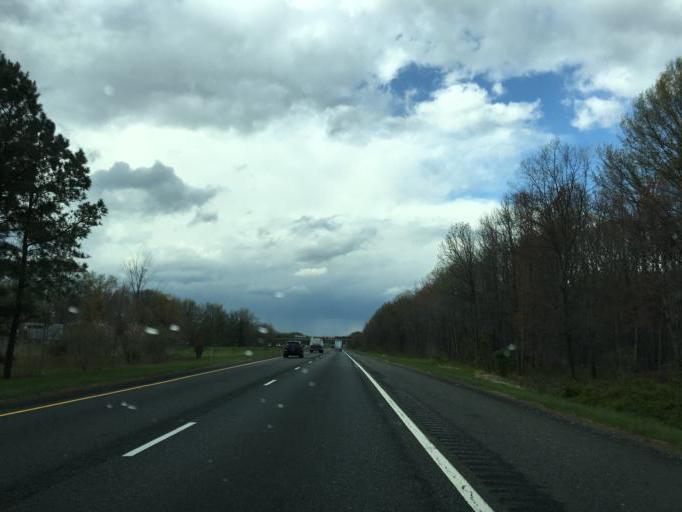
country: US
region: Maryland
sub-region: Baltimore County
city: Edgemere
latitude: 39.2671
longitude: -76.4610
